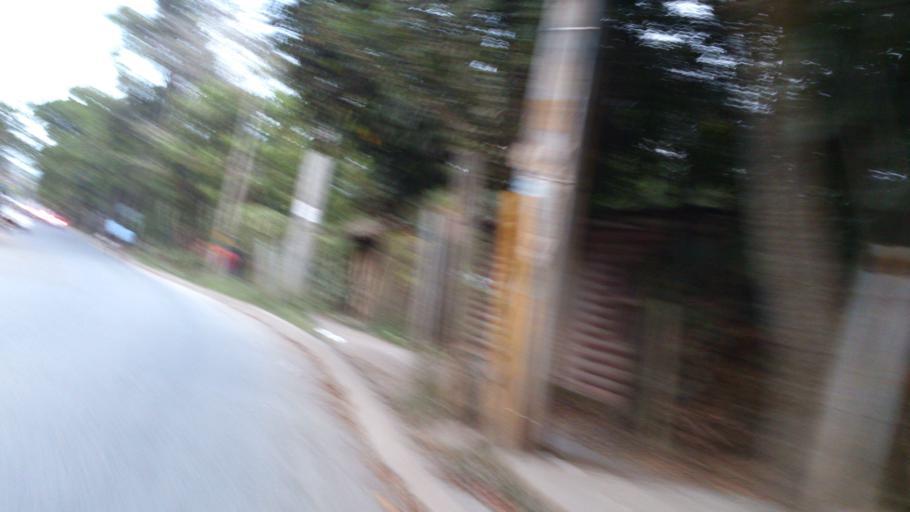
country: CO
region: Valle del Cauca
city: Jamundi
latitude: 3.2567
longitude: -76.5468
